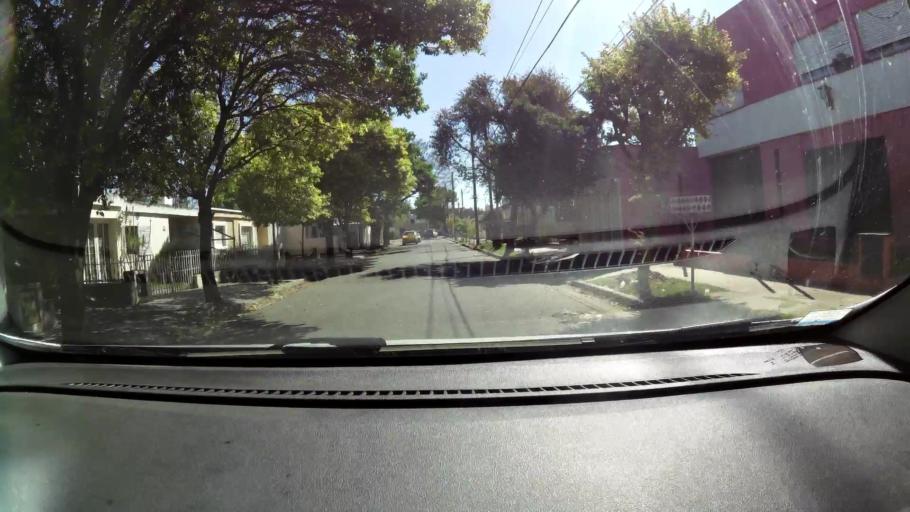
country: AR
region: Cordoba
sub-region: Departamento de Capital
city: Cordoba
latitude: -31.3746
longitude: -64.1698
